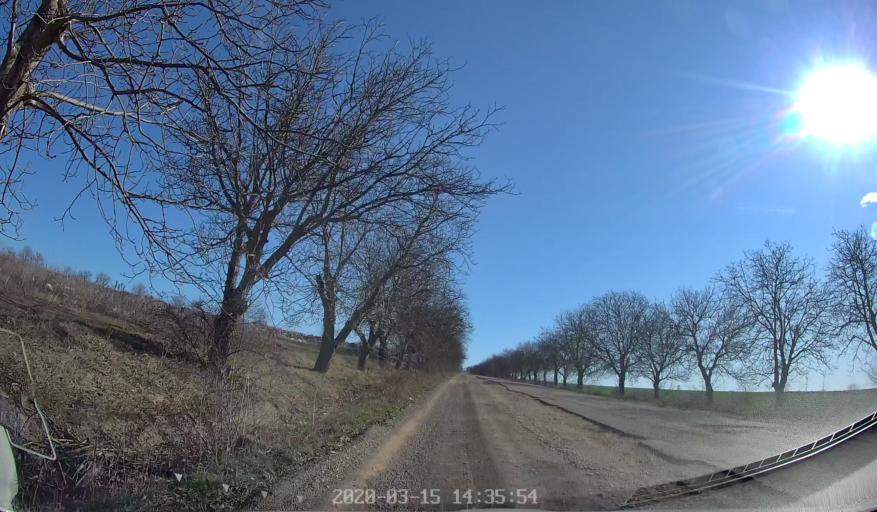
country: MD
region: Orhei
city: Orhei
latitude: 47.3277
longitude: 28.9250
